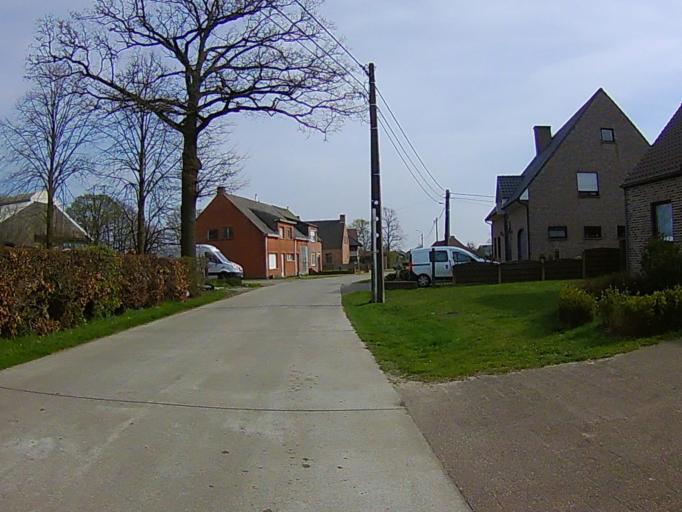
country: BE
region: Flanders
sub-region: Provincie Antwerpen
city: Kasterlee
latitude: 51.2201
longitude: 4.9366
